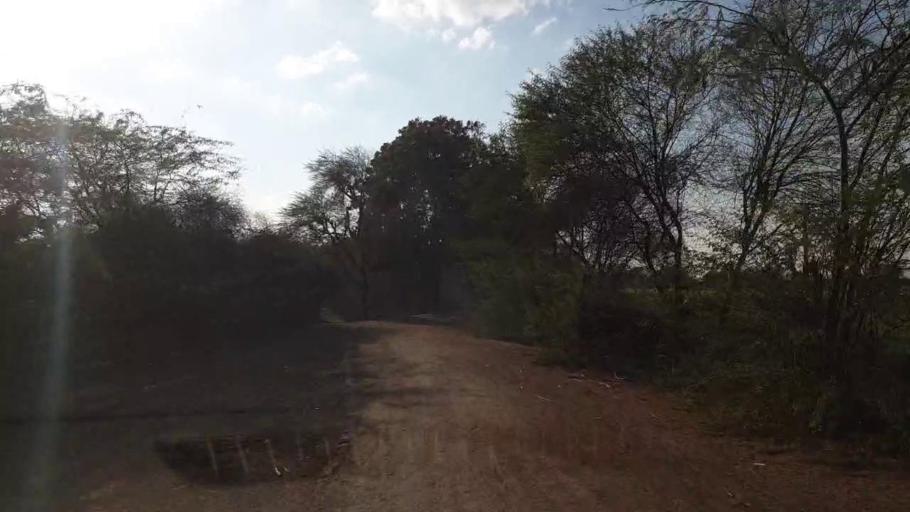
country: PK
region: Sindh
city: Shahpur Chakar
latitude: 26.1241
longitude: 68.5647
